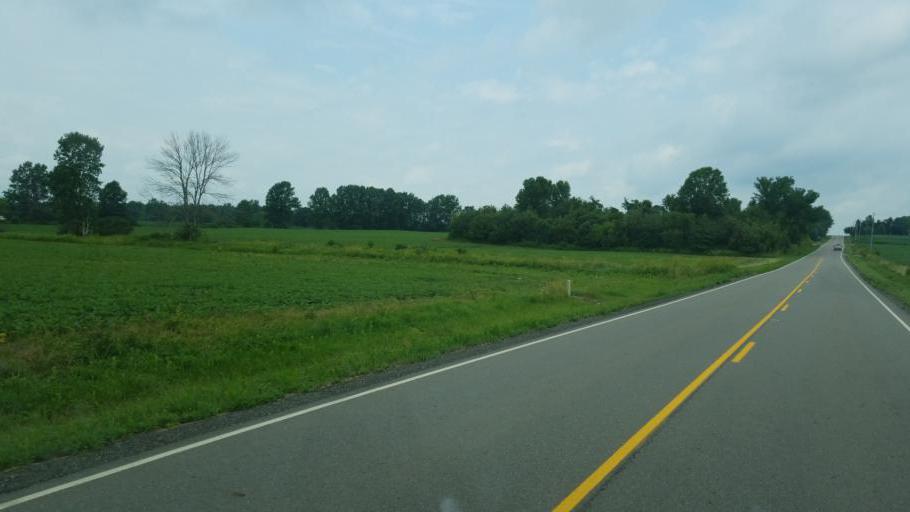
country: US
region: Ohio
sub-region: Licking County
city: Utica
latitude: 40.1942
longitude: -82.5180
